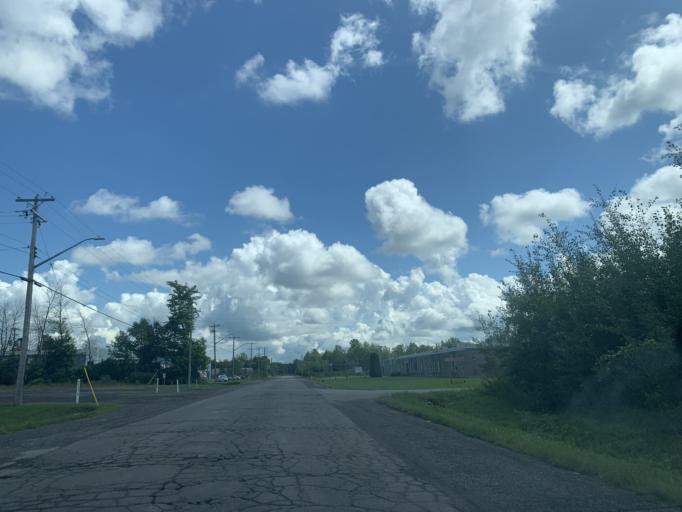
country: CA
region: Ontario
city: Hawkesbury
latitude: 45.6012
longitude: -74.5942
